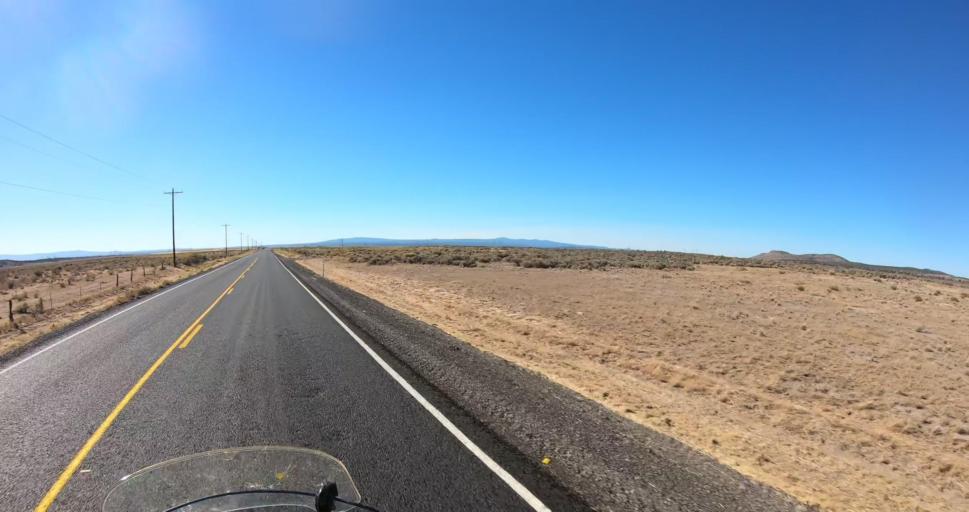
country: US
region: Oregon
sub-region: Deschutes County
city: La Pine
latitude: 43.1308
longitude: -120.9229
